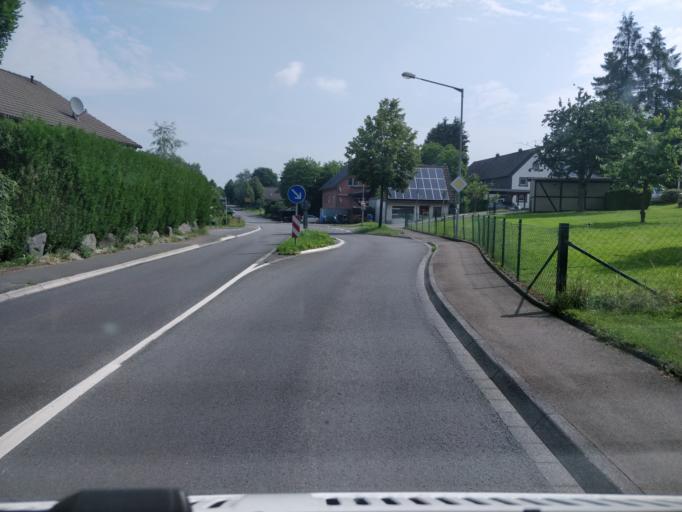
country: DE
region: North Rhine-Westphalia
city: Wiehl
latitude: 50.9330
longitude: 7.5755
